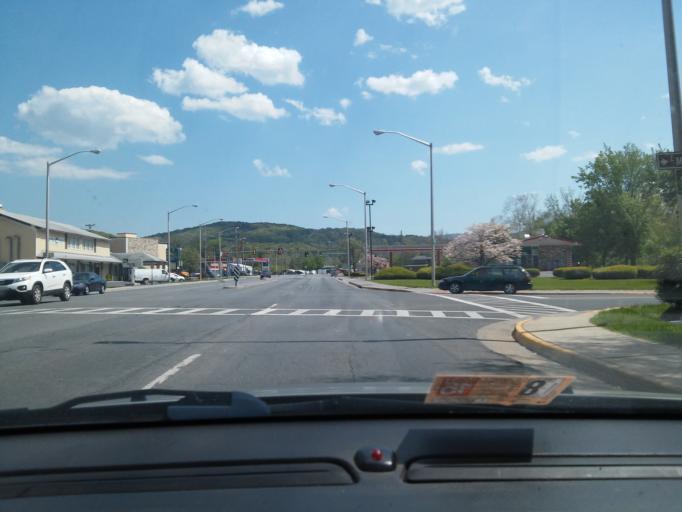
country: US
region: Virginia
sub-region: Warren County
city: Front Royal
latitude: 38.9174
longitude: -78.1869
